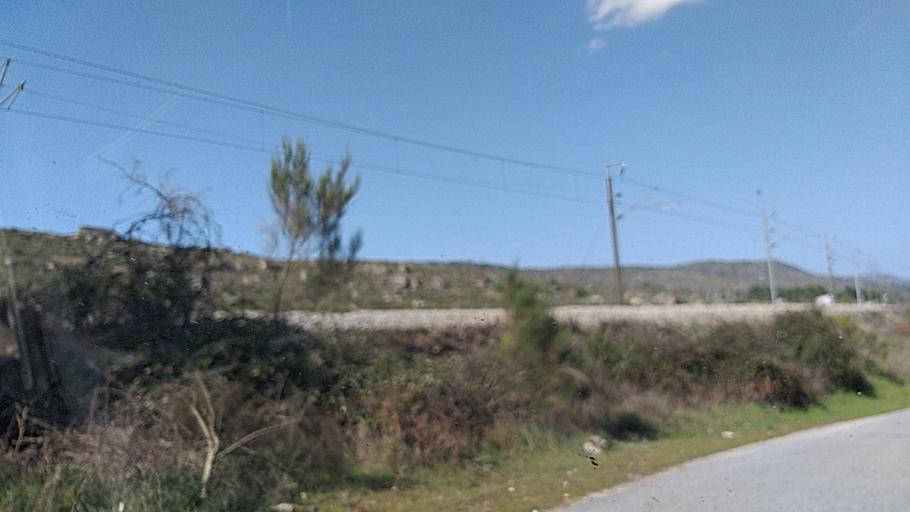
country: PT
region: Guarda
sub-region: Celorico da Beira
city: Celorico da Beira
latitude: 40.6333
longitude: -7.4345
